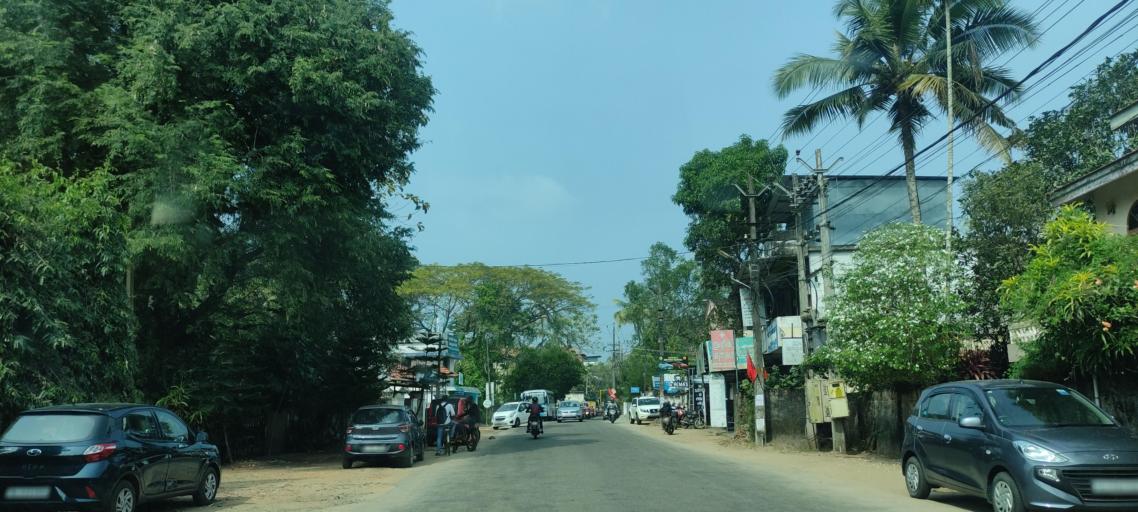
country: IN
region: Kerala
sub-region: Alappuzha
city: Shertallai
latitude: 9.6837
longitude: 76.3445
